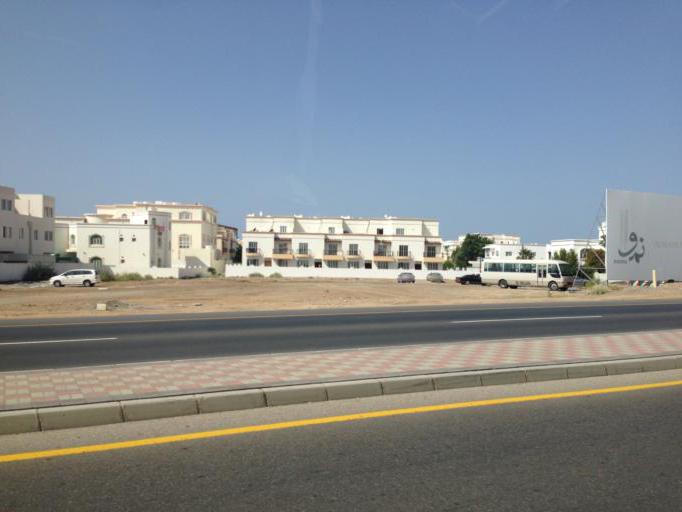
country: OM
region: Muhafazat Masqat
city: Bawshar
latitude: 23.5992
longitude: 58.3822
